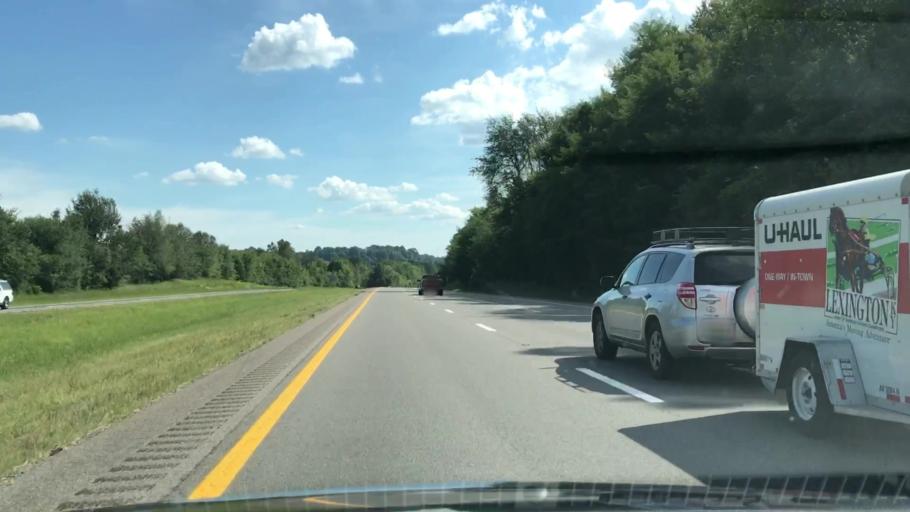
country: US
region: Tennessee
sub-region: Marshall County
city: Cornersville
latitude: 35.3016
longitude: -86.8827
